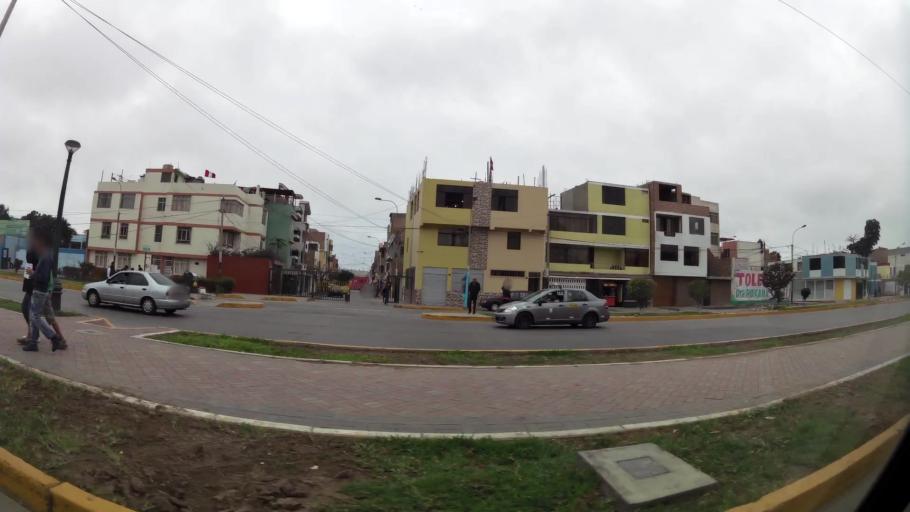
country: PE
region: Callao
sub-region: Callao
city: Callao
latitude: -12.0604
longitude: -77.1155
